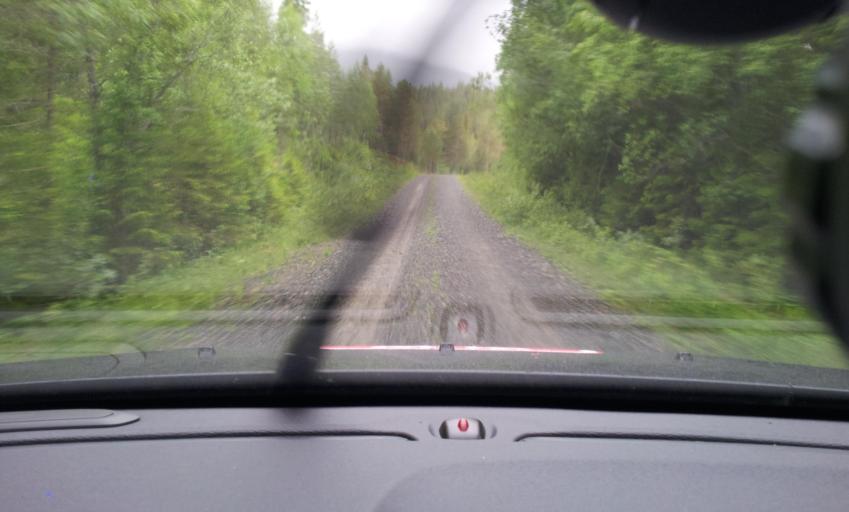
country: SE
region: Jaemtland
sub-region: Are Kommun
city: Jarpen
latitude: 63.1917
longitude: 13.4140
